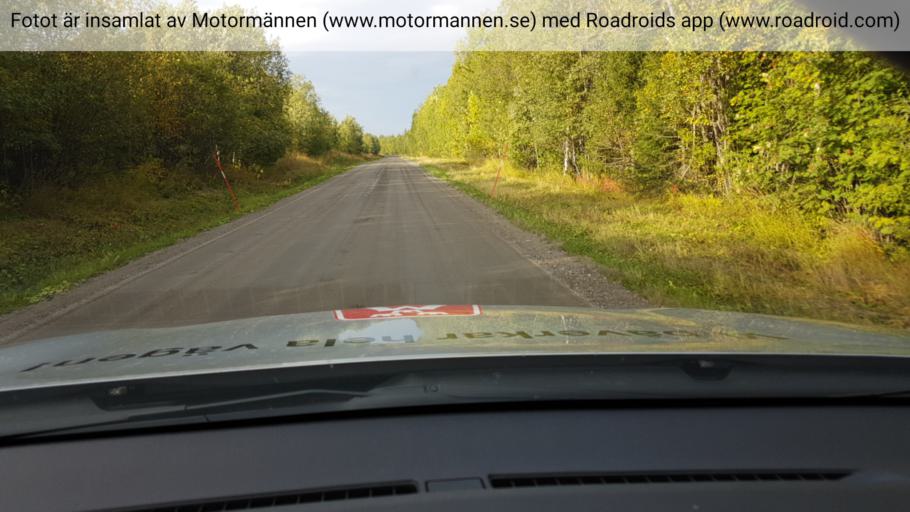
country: SE
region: Jaemtland
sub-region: Stroemsunds Kommun
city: Stroemsund
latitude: 64.0109
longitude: 15.8152
